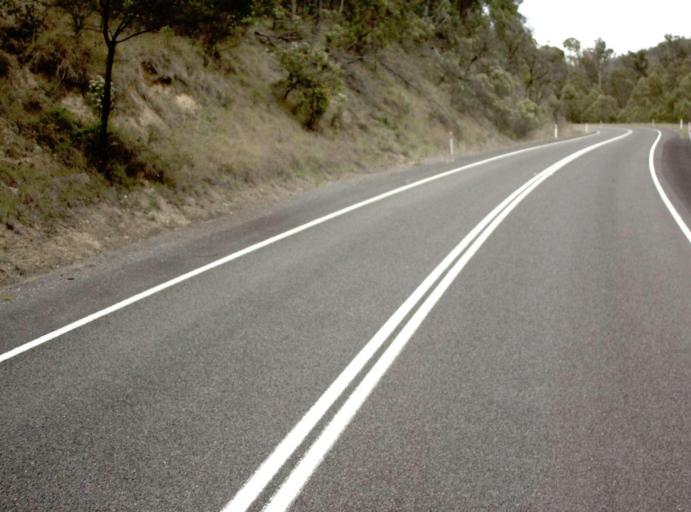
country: AU
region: New South Wales
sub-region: Bombala
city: Bombala
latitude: -37.2574
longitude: 149.2410
